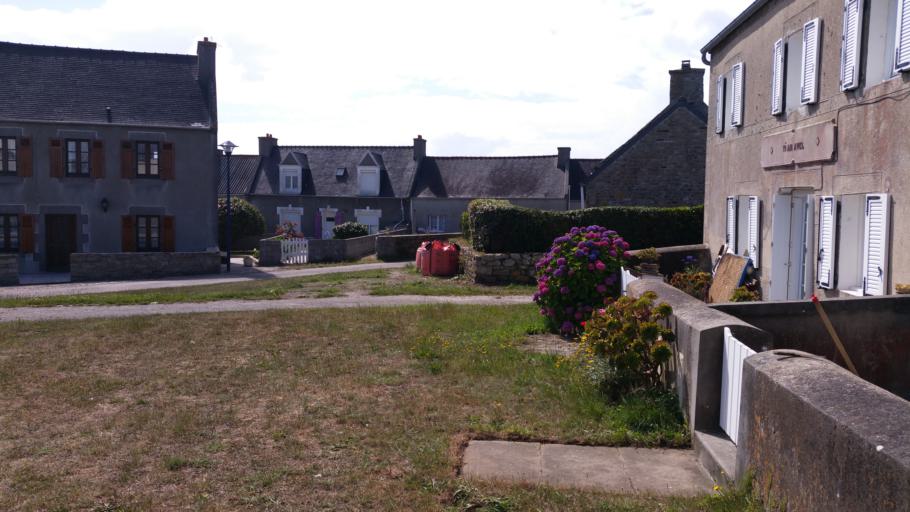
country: FR
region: Brittany
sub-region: Departement du Finistere
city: Le Conquet
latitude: 48.3963
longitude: -4.9572
